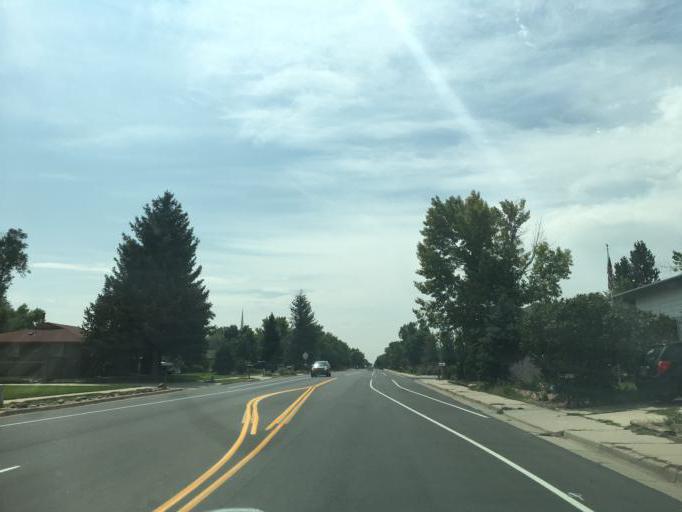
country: US
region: Colorado
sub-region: Adams County
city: Aurora
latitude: 39.7335
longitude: -104.8007
